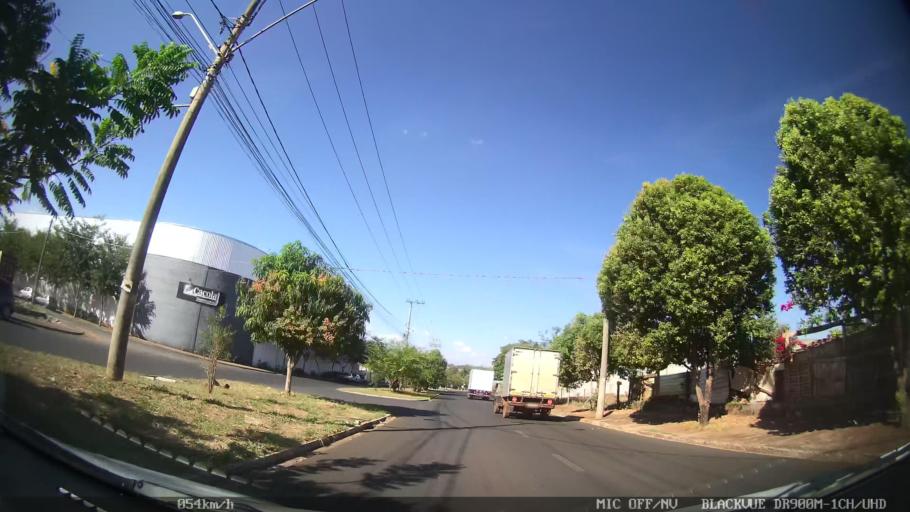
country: BR
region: Sao Paulo
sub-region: Ribeirao Preto
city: Ribeirao Preto
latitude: -21.1529
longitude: -47.7591
